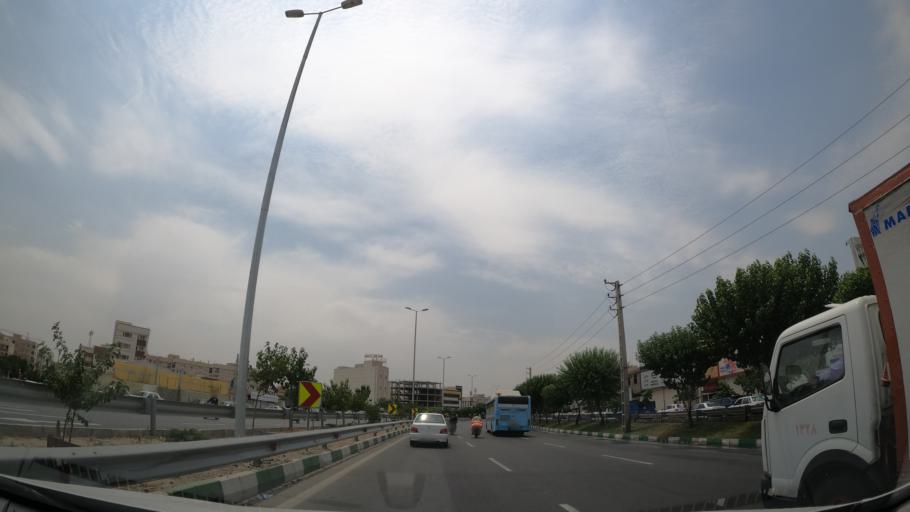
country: IR
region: Tehran
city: Tehran
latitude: 35.6758
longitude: 51.3266
